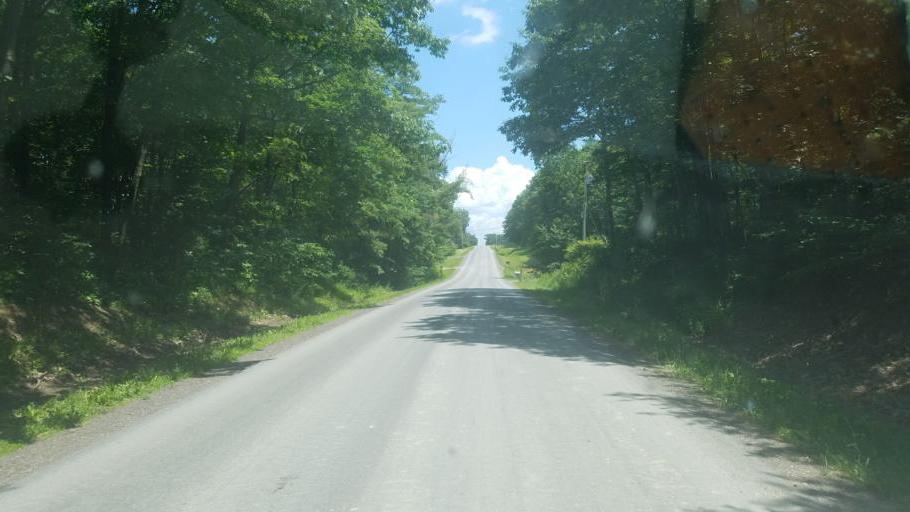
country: US
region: New York
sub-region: Yates County
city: Keuka Park
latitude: 42.5930
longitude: -77.0329
